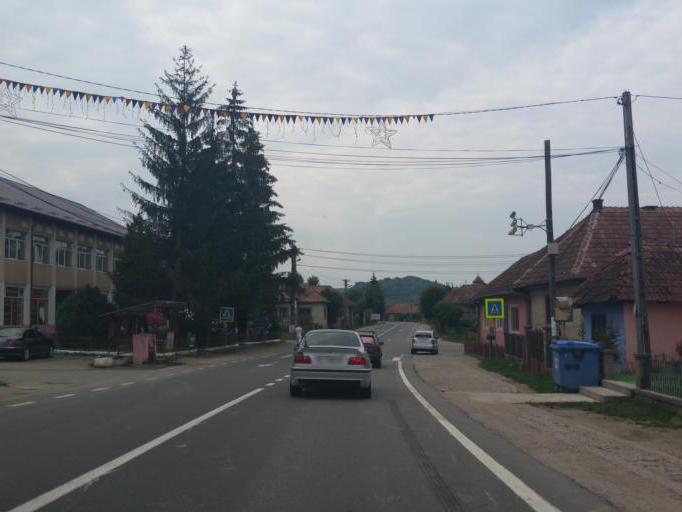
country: RO
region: Salaj
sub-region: Comuna Hida
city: Hida
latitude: 47.0365
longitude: 23.2674
